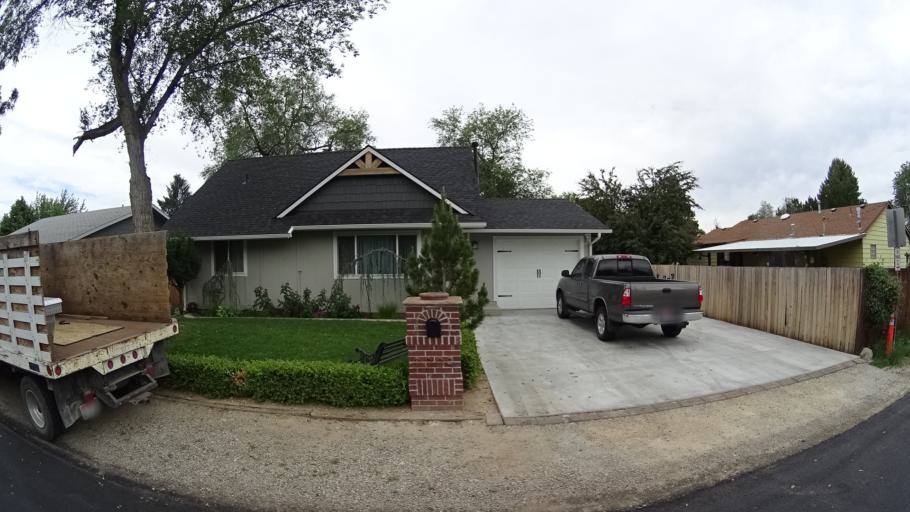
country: US
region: Idaho
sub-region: Ada County
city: Boise
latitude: 43.5824
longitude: -116.2037
